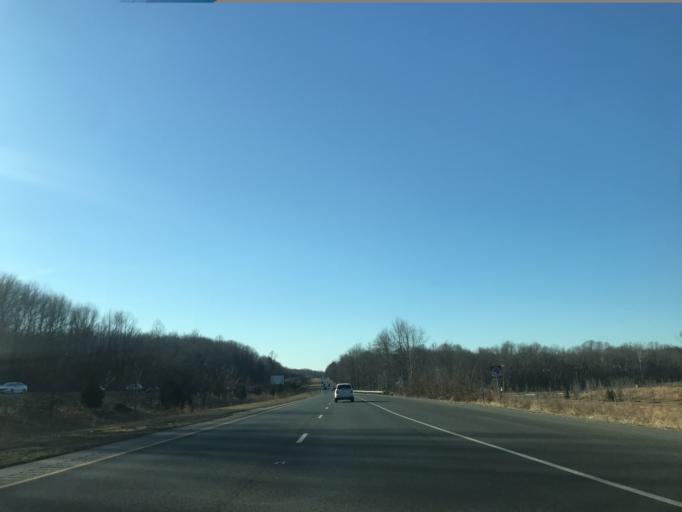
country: US
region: Maryland
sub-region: Prince George's County
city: Mellwood
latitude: 38.8160
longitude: -76.8311
